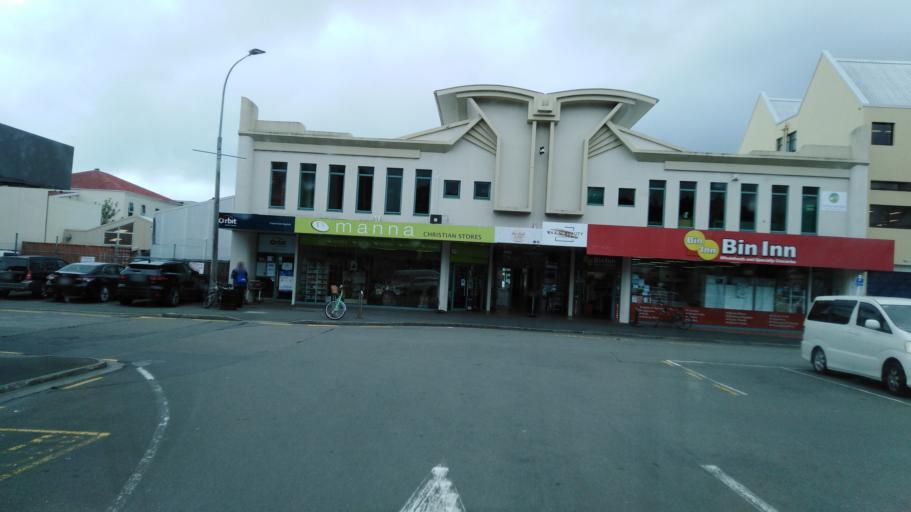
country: NZ
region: Nelson
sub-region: Nelson City
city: Nelson
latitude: -41.2732
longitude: 173.2819
